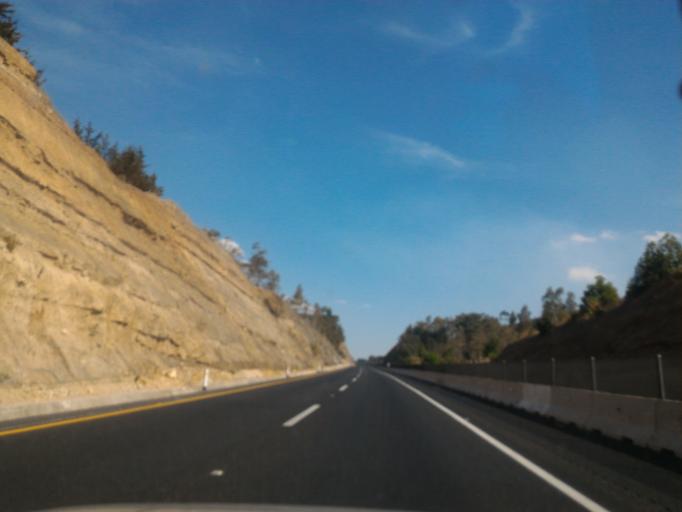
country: MX
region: Mexico
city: Temascalcingo de Jose Maria Velazco
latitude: 19.8533
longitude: -100.0249
